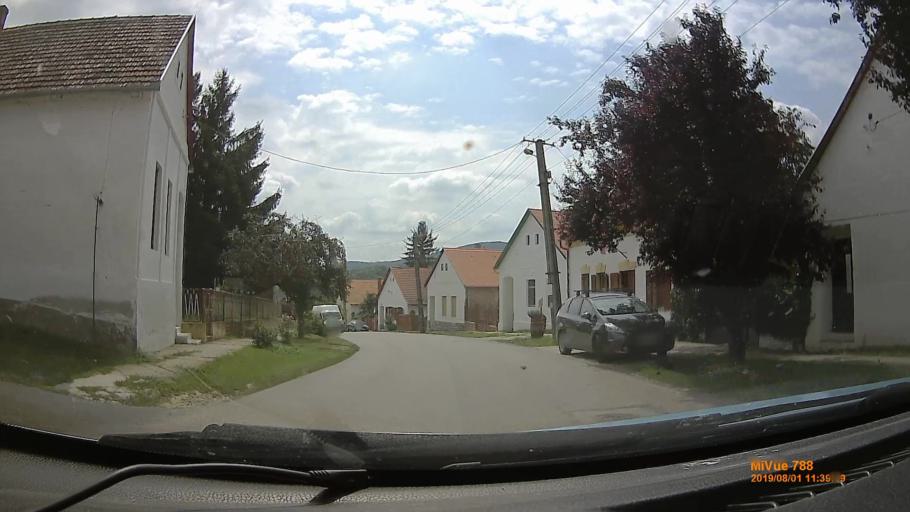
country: HU
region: Baranya
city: Villany
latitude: 45.8955
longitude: 18.3907
